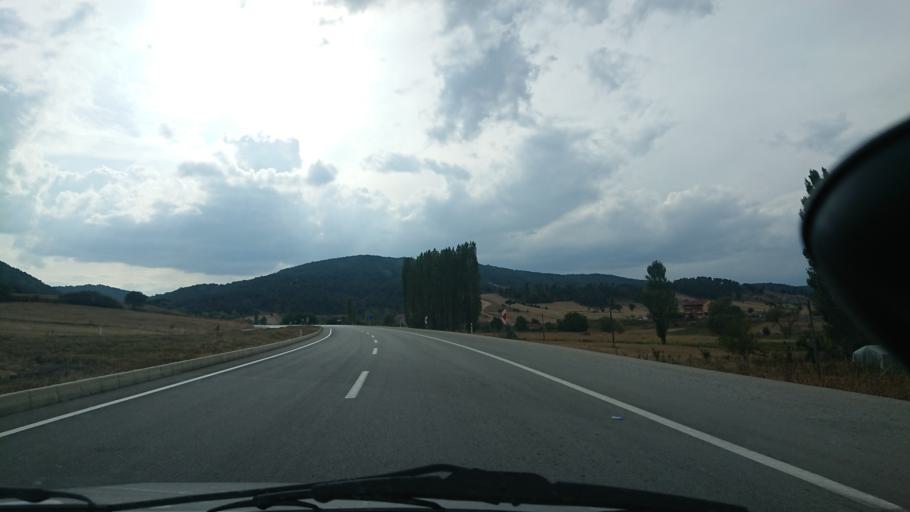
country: TR
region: Kuetahya
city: Gediz
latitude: 39.1044
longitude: 29.4869
